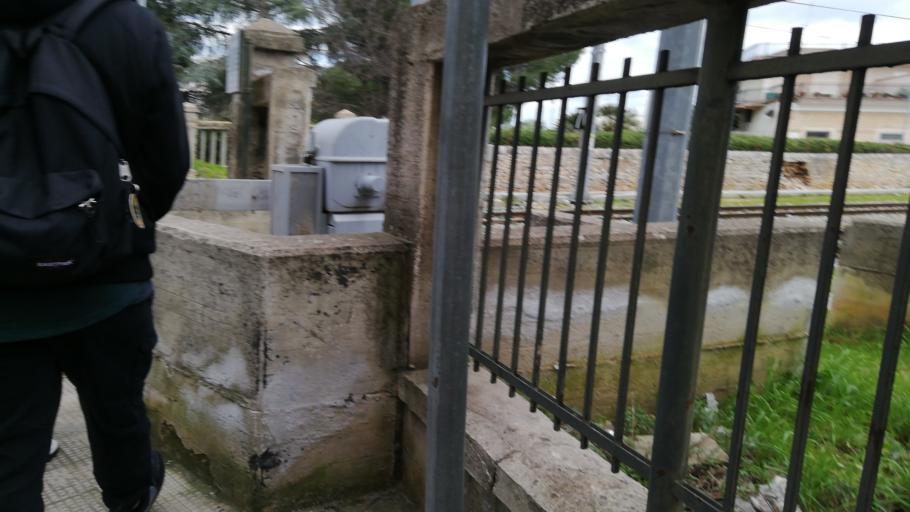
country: IT
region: Apulia
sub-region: Provincia di Bari
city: Bitonto
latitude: 41.1127
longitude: 16.6832
